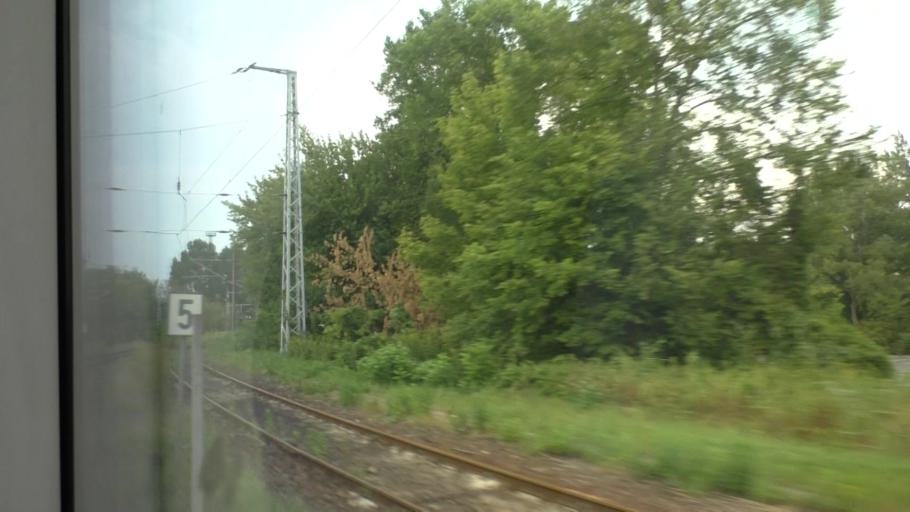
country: DE
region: Brandenburg
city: Konigs Wusterhausen
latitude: 52.2984
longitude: 13.6316
